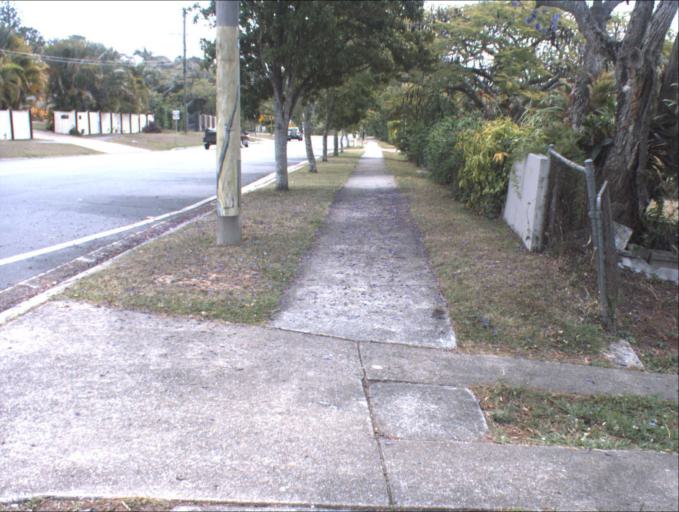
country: AU
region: Queensland
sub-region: Logan
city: Slacks Creek
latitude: -27.6502
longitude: 153.1629
